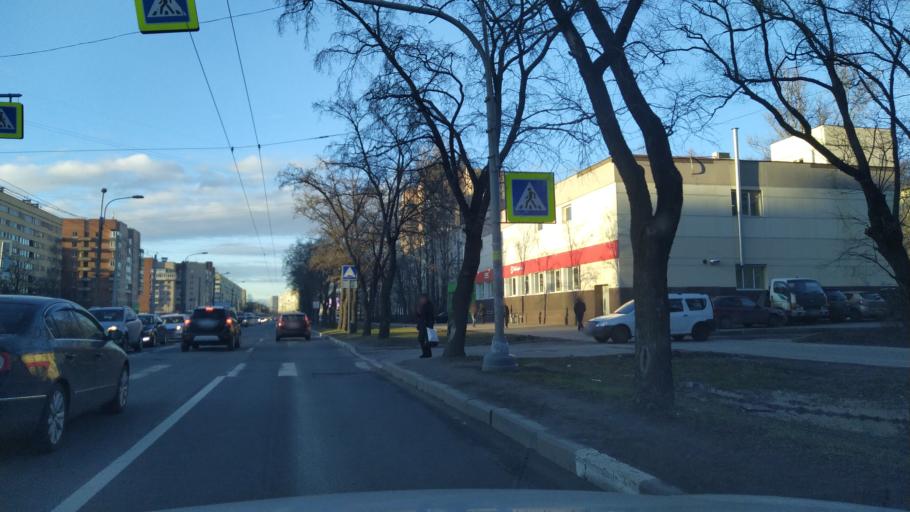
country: RU
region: St.-Petersburg
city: Dachnoye
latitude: 59.8492
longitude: 30.2563
